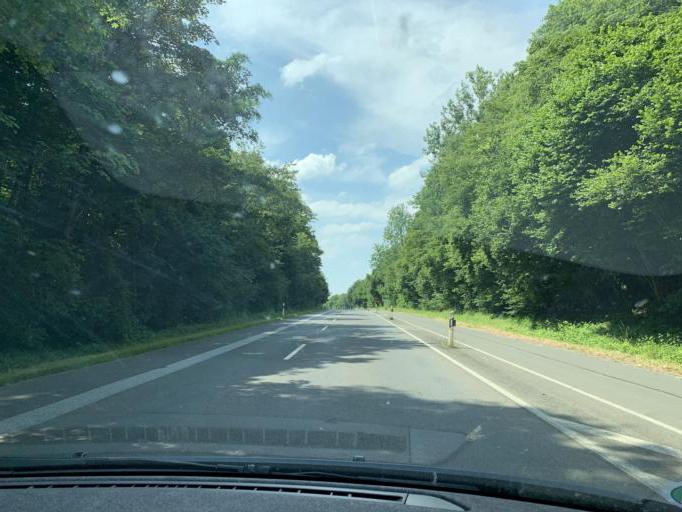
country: DE
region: North Rhine-Westphalia
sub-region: Regierungsbezirk Koln
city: Bedburg
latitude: 51.0202
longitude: 6.6158
